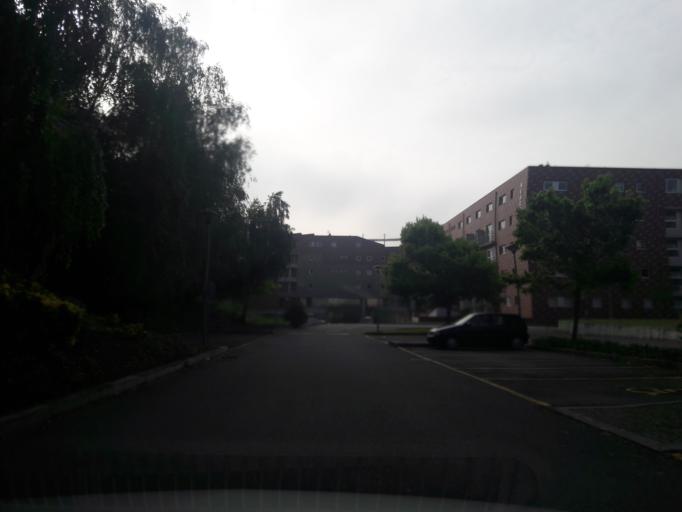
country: PT
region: Porto
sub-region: Porto
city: Porto
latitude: 41.1513
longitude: -8.6320
